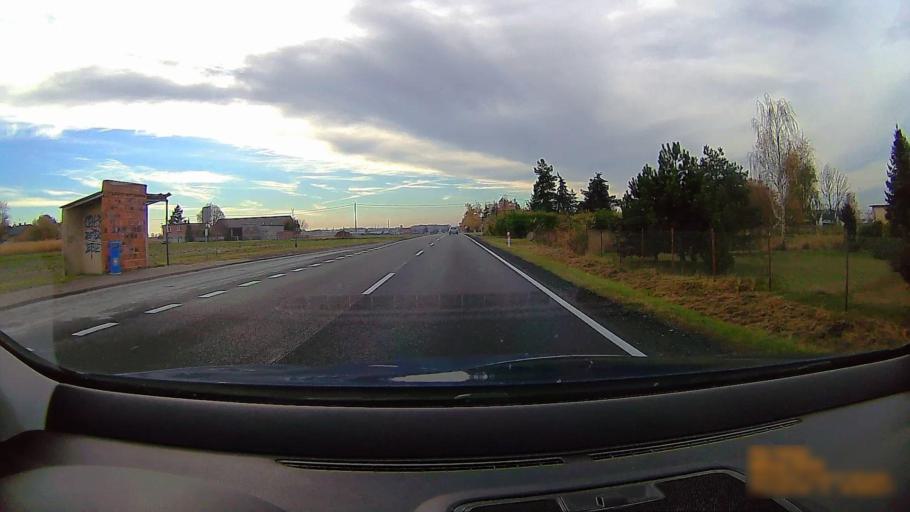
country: PL
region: Greater Poland Voivodeship
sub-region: Kalisz
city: Kalisz
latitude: 51.8336
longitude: 18.0953
